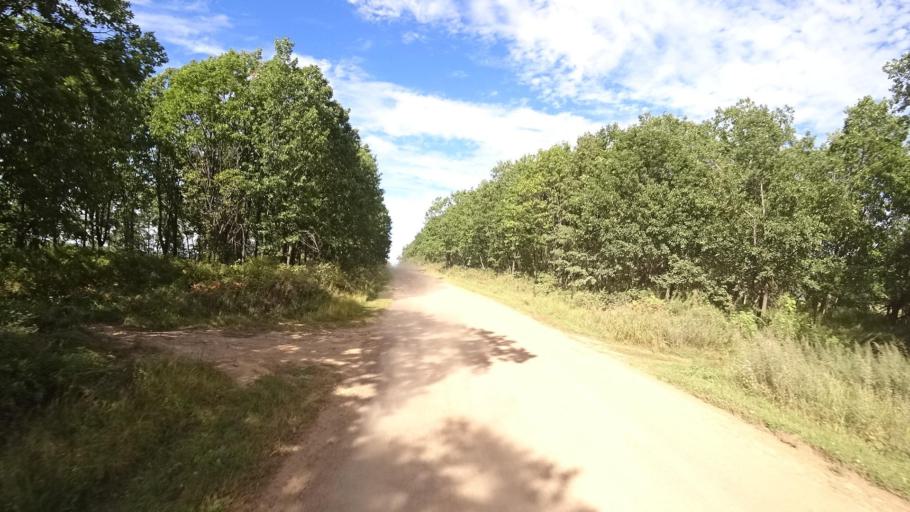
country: RU
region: Primorskiy
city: Yakovlevka
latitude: 44.4120
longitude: 133.5697
